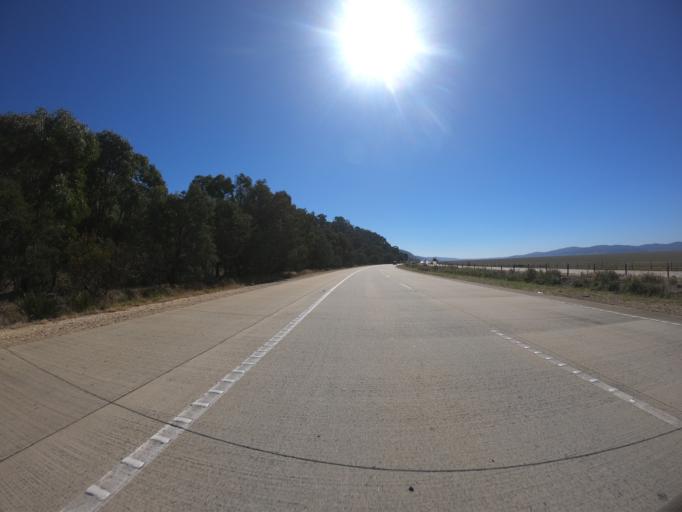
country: AU
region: New South Wales
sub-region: Yass Valley
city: Gundaroo
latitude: -35.0889
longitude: 149.3745
